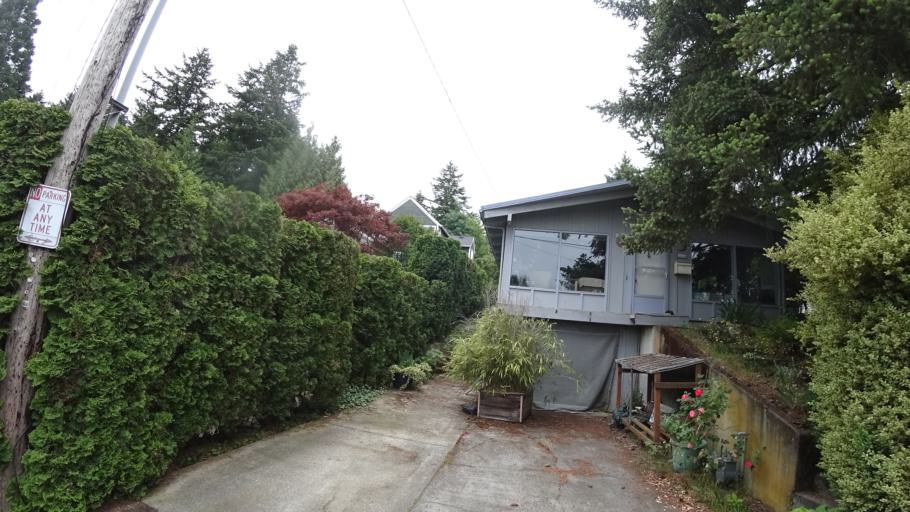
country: US
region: Oregon
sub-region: Multnomah County
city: Portland
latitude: 45.4981
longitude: -122.6934
